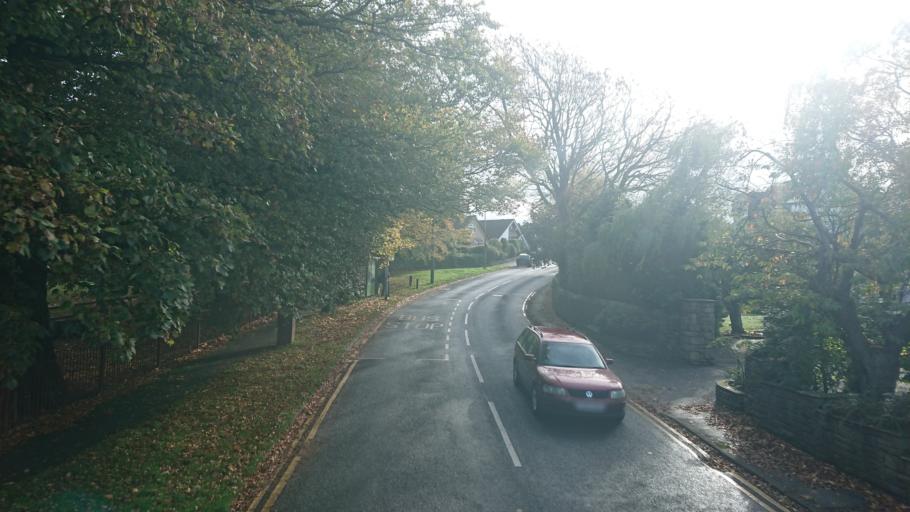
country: GB
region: England
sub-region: Lancashire
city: Bolton le Sands
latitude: 54.0853
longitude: -2.8083
